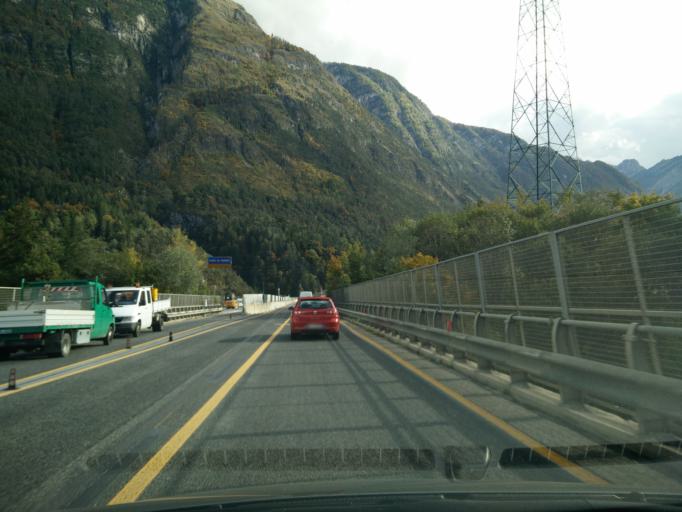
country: IT
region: Veneto
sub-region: Provincia di Belluno
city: Perarolo di Cadore
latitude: 46.4049
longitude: 12.3703
